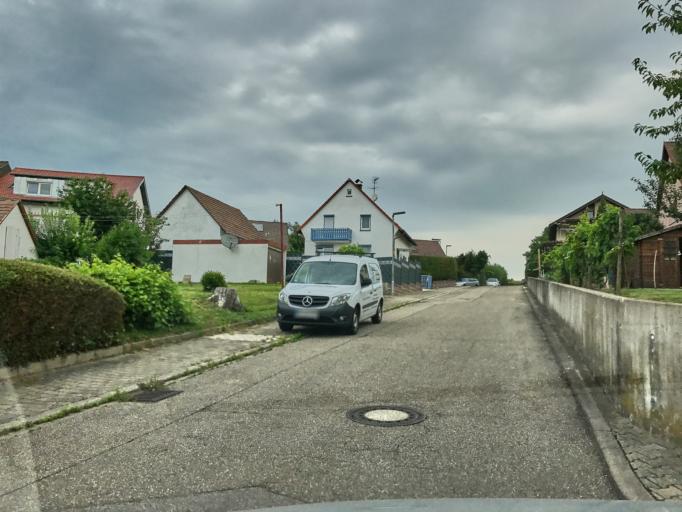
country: DE
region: Baden-Wuerttemberg
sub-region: Karlsruhe Region
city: Joehlingen
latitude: 49.0297
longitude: 8.5846
